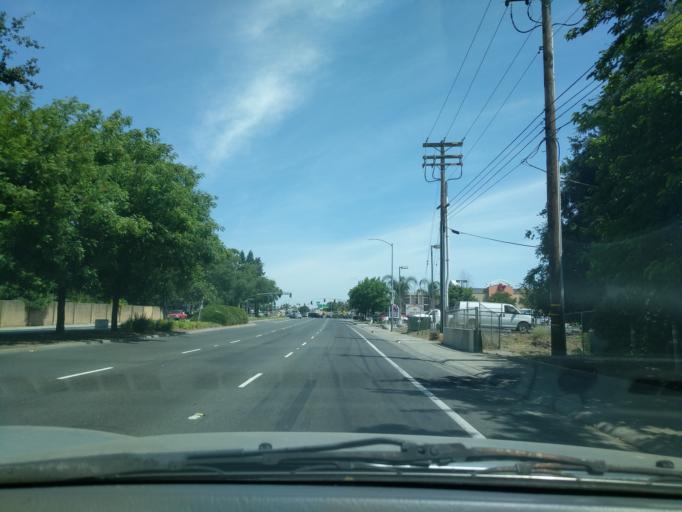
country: US
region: California
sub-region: Sacramento County
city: La Riviera
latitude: 38.5605
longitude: -121.3361
